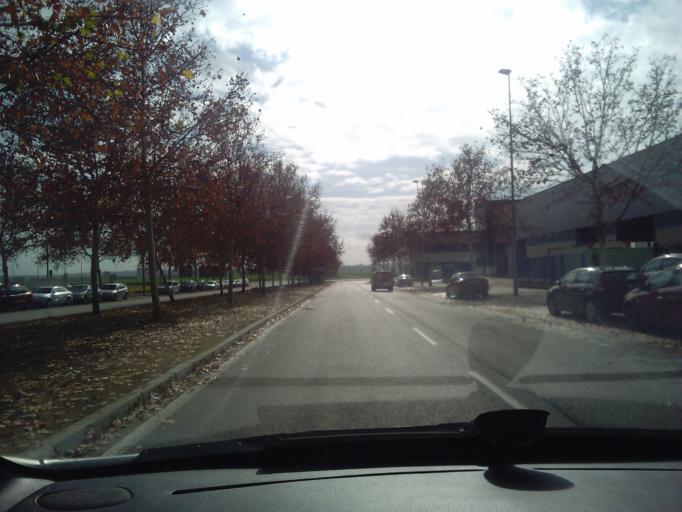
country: ES
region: Andalusia
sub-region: Provincia de Sevilla
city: Sevilla
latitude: 37.3754
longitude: -5.9194
